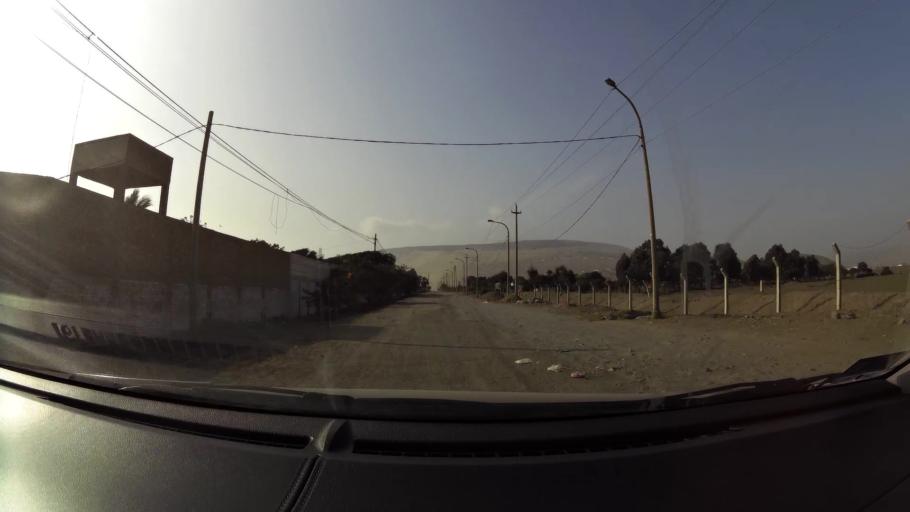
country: PE
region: Lima
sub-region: Lima
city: Santa Rosa
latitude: -11.7579
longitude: -77.1694
